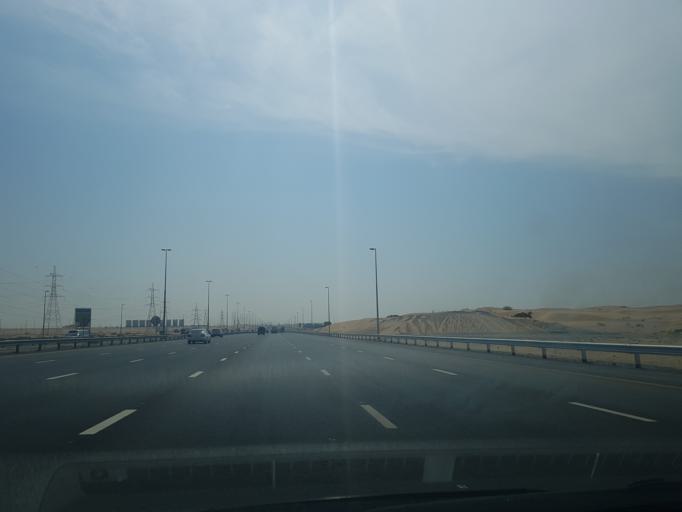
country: AE
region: Ash Shariqah
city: Sharjah
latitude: 25.2780
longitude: 55.5842
